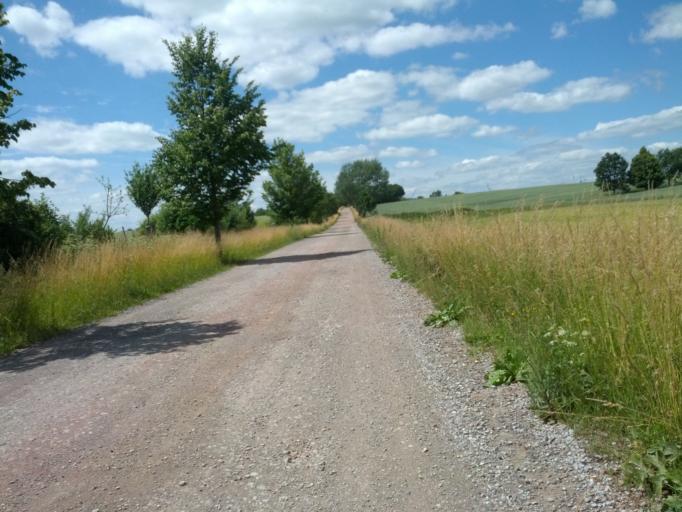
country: DE
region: Thuringia
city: Bischofroda
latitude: 51.0166
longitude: 10.3474
